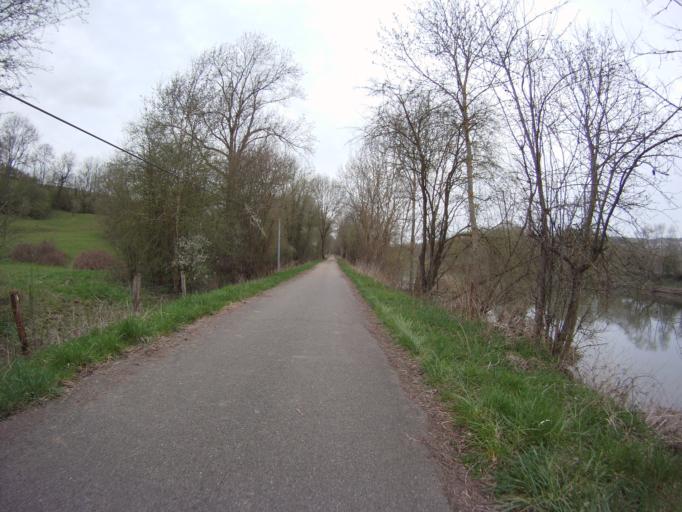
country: FR
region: Lorraine
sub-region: Departement de Meurthe-et-Moselle
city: Chaligny
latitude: 48.6123
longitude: 6.0840
